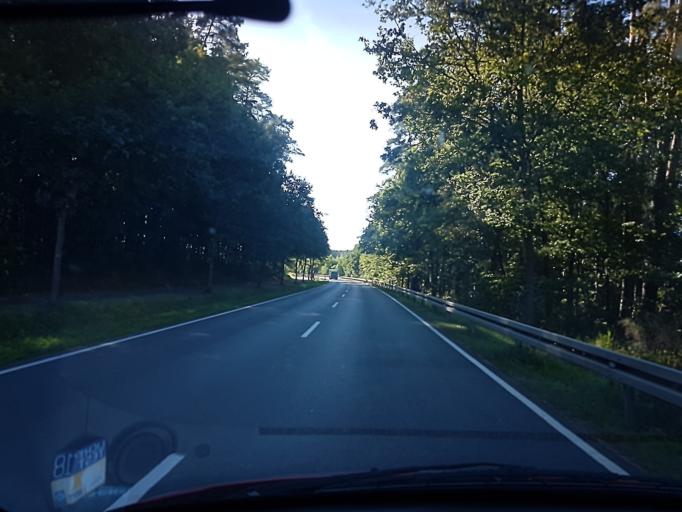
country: DE
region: Bavaria
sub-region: Upper Franconia
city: Heroldsbach
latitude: 49.7090
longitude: 10.9967
